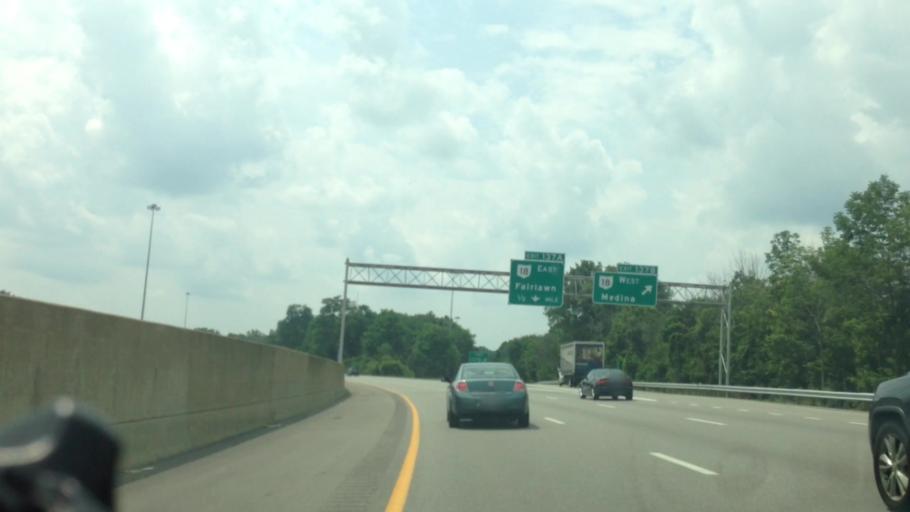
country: US
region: Ohio
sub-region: Summit County
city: Montrose-Ghent
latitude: 41.1412
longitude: -81.6477
